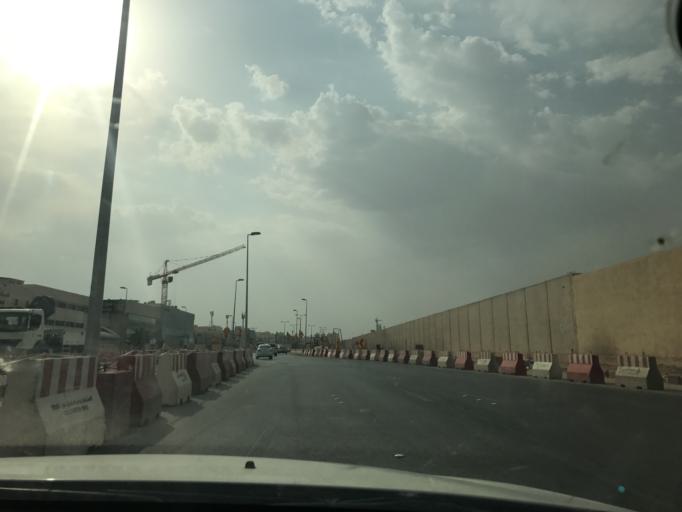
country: SA
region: Ar Riyad
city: Riyadh
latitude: 24.7088
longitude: 46.7109
